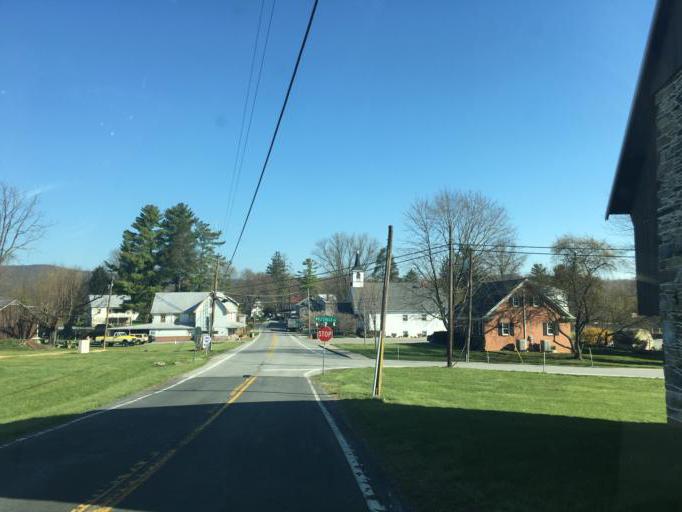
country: US
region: Maryland
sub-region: Frederick County
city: Myersville
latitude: 39.5728
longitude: -77.5509
